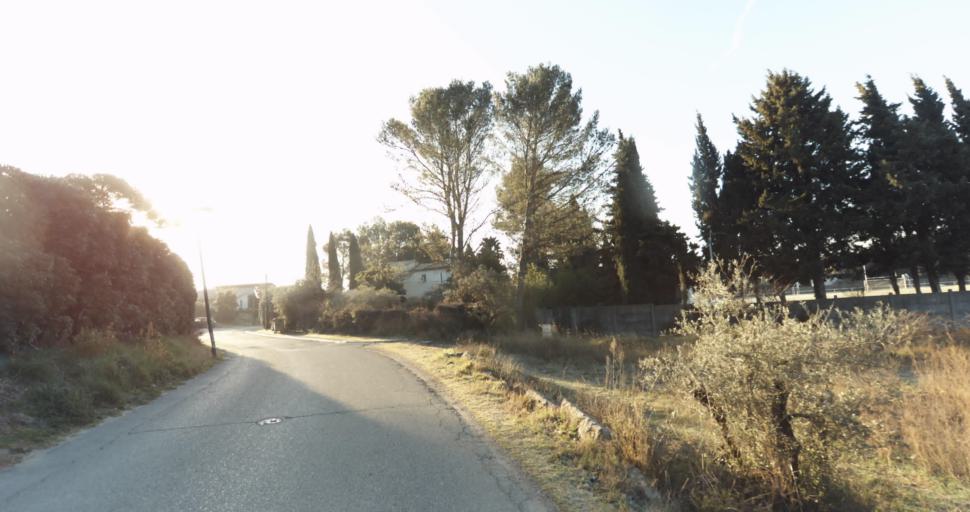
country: FR
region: Provence-Alpes-Cote d'Azur
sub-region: Departement des Bouches-du-Rhone
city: Barbentane
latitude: 43.8961
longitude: 4.7442
